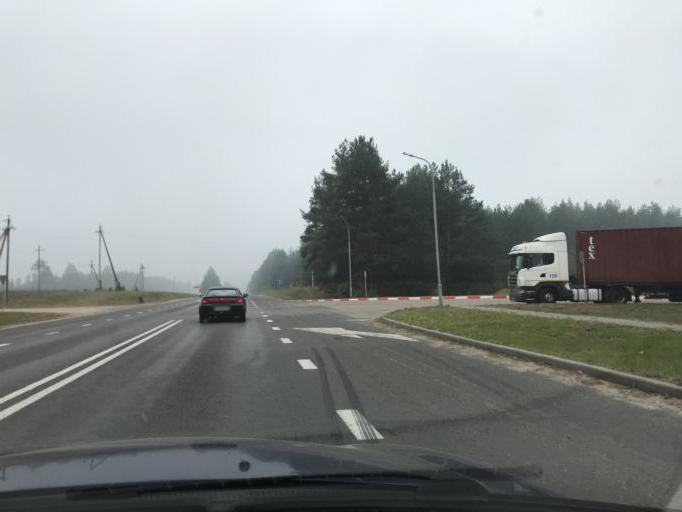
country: BY
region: Grodnenskaya
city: Hrodna
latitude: 53.8054
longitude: 23.8605
